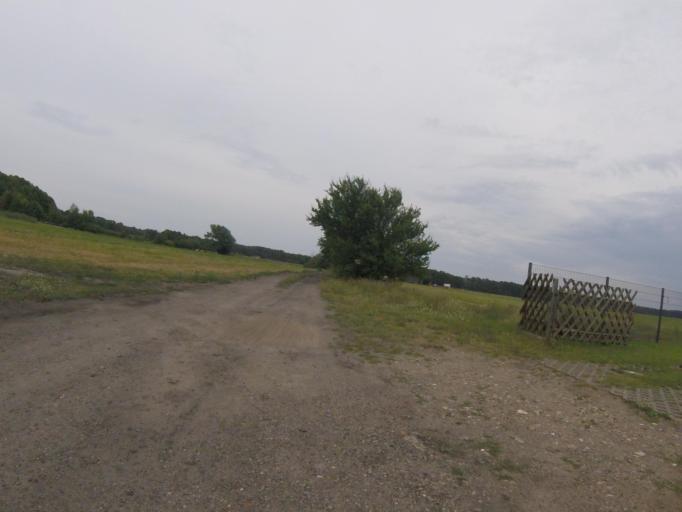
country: DE
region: Brandenburg
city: Gross Koris
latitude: 52.1683
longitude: 13.7067
